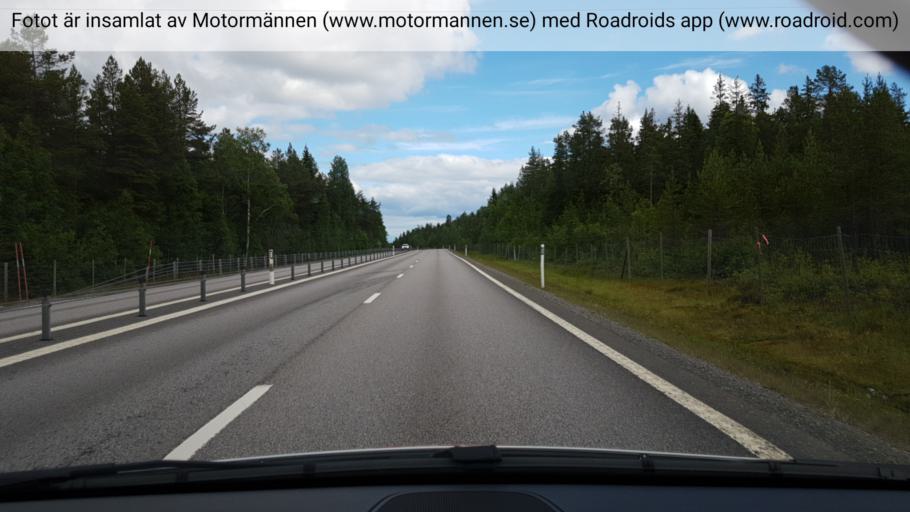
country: SE
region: Norrbotten
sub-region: Pitea Kommun
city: Pitea
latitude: 65.1718
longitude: 21.4988
